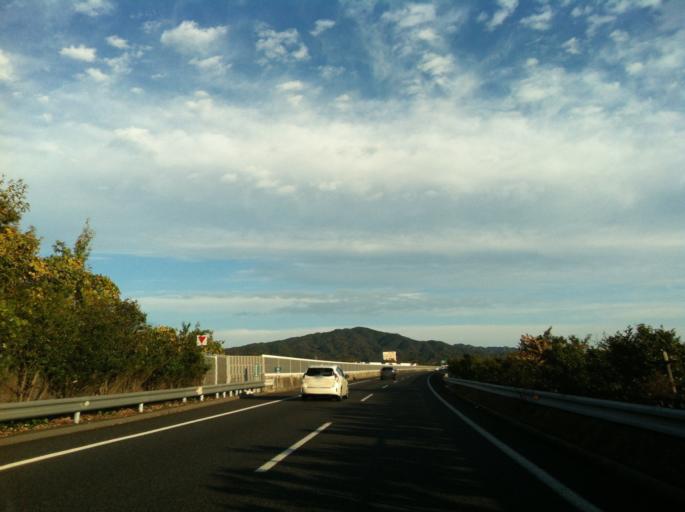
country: JP
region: Aichi
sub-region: Toyota-shi
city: Toyota
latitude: 35.1496
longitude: 137.1791
